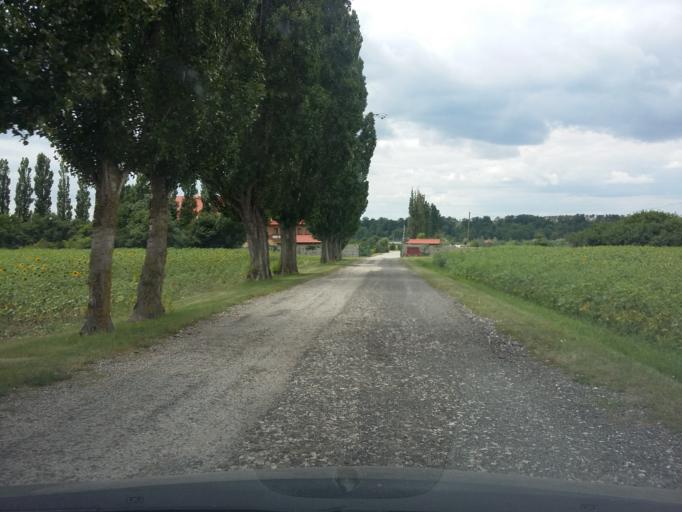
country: SK
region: Trnavsky
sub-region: Okres Senica
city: Senica
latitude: 48.5810
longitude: 17.3517
